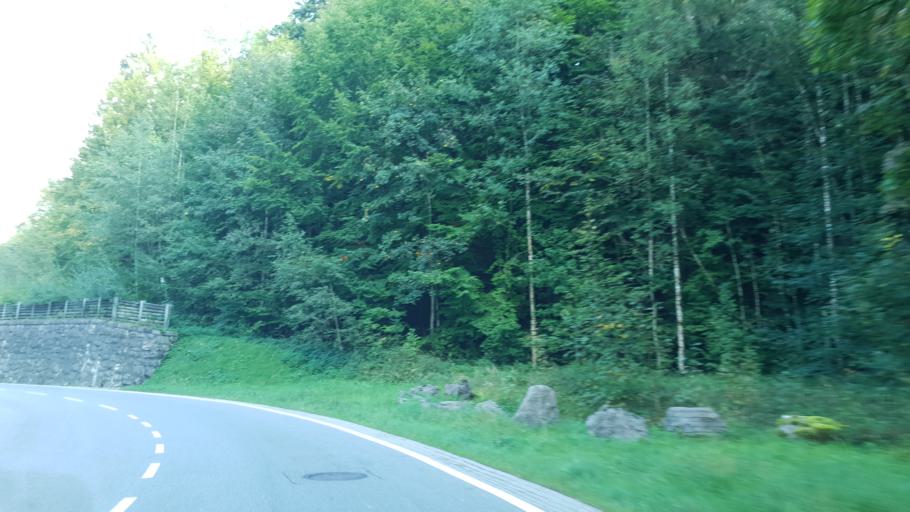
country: AT
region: Vorarlberg
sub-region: Politischer Bezirk Bregenz
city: Andelsbuch
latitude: 47.4011
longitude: 9.8710
